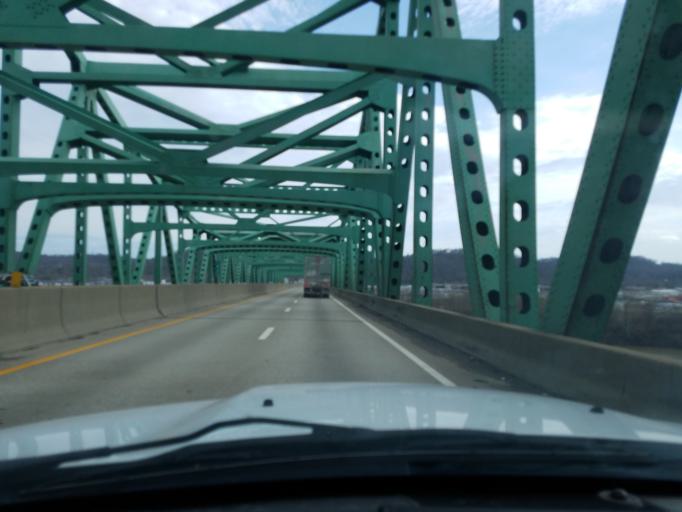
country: US
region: West Virginia
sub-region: Kanawha County
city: Nitro
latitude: 38.4456
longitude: -81.8436
